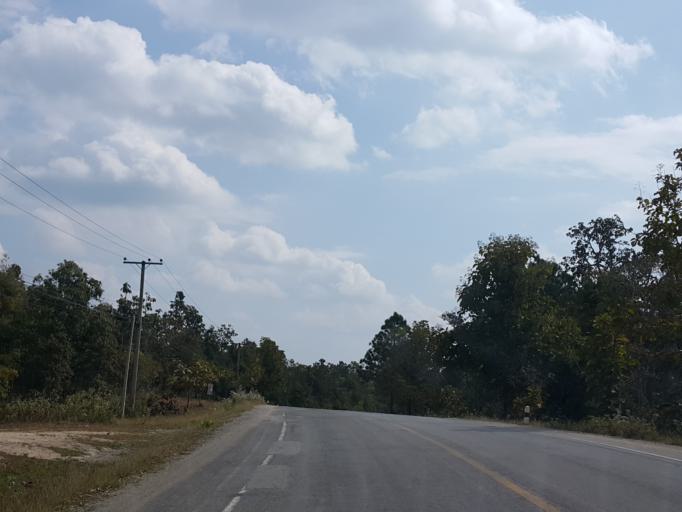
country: TH
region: Chiang Mai
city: Om Koi
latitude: 17.8443
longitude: 98.3727
